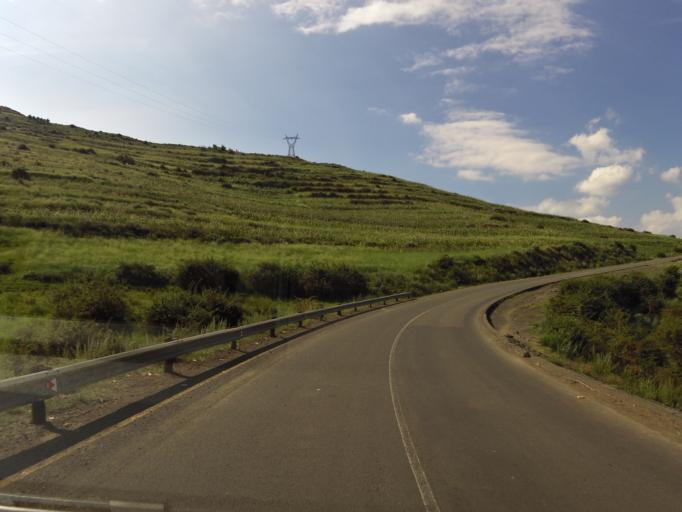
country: LS
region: Thaba-Tseka
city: Thaba-Tseka
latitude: -29.1235
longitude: 28.4913
